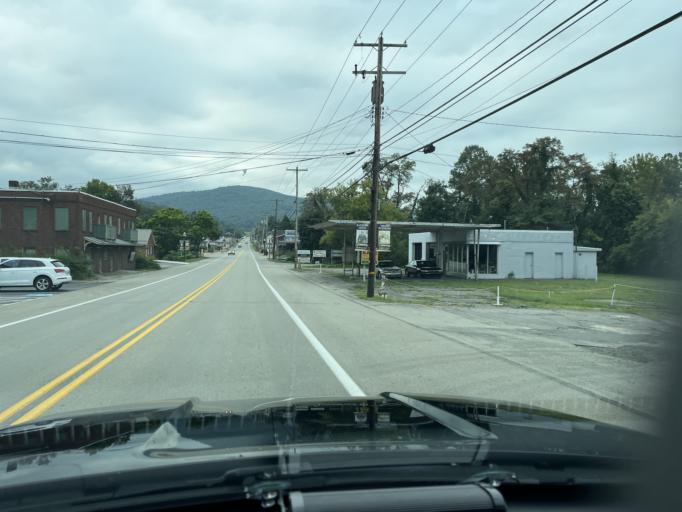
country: US
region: Pennsylvania
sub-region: Fayette County
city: Hopwood
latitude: 39.8791
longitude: -79.7032
